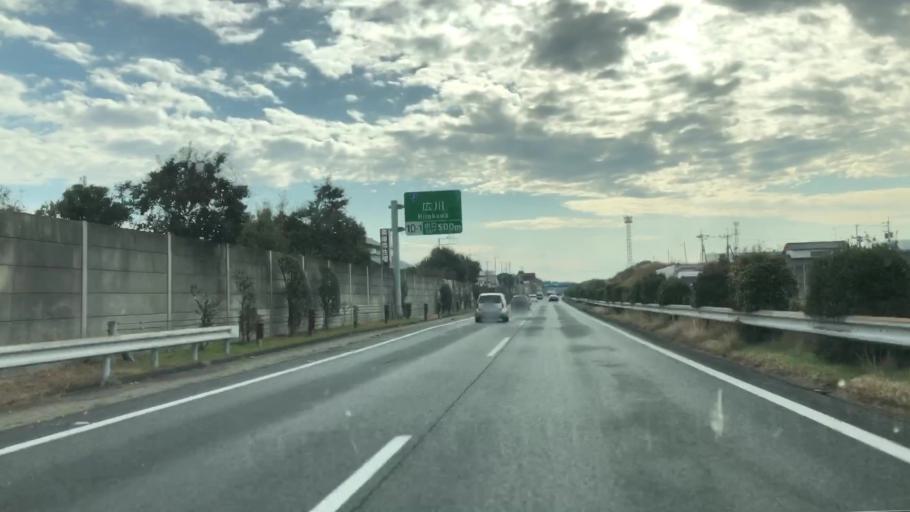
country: JP
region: Fukuoka
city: Kurume
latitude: 33.2621
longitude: 130.5384
